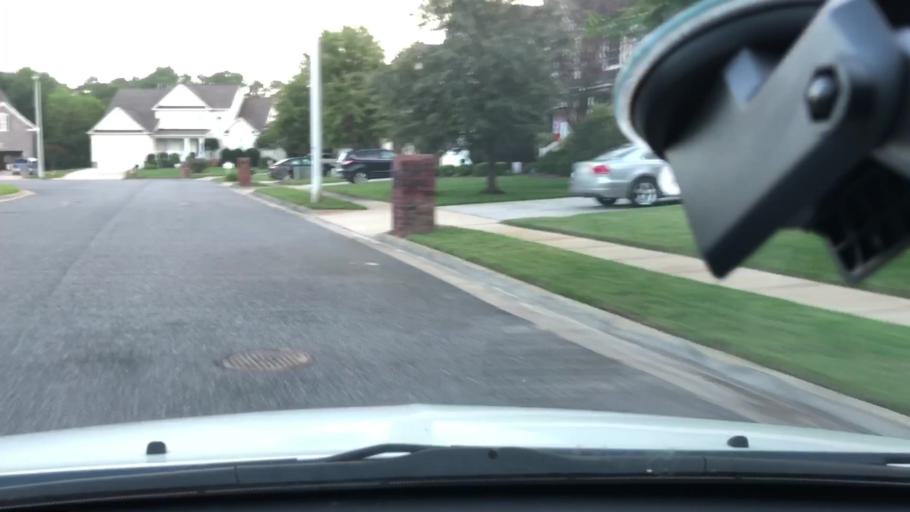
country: US
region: Virginia
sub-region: City of Chesapeake
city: Chesapeake
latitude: 36.7274
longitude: -76.2841
